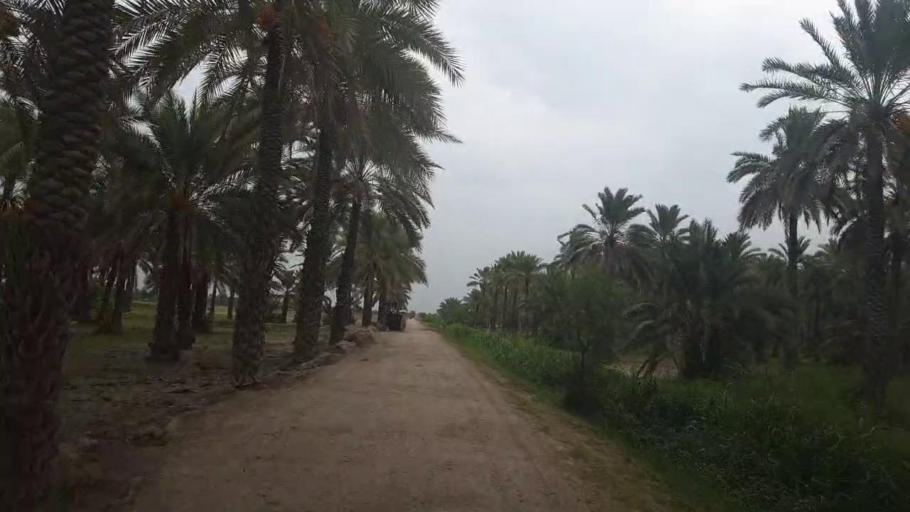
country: PK
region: Sindh
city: Khairpur
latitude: 27.5613
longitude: 68.7110
